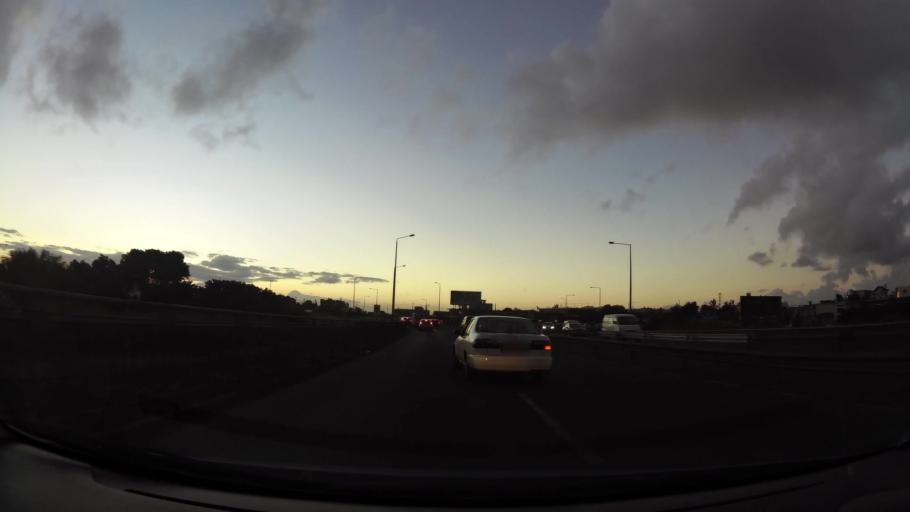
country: MU
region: Plaines Wilhems
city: Curepipe
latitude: -20.2879
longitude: 57.5253
